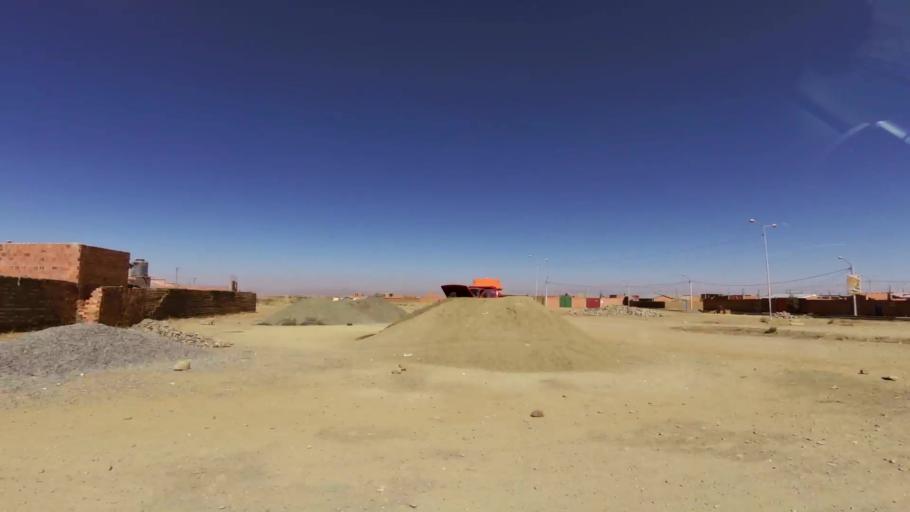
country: BO
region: La Paz
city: La Paz
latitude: -16.6016
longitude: -68.2025
